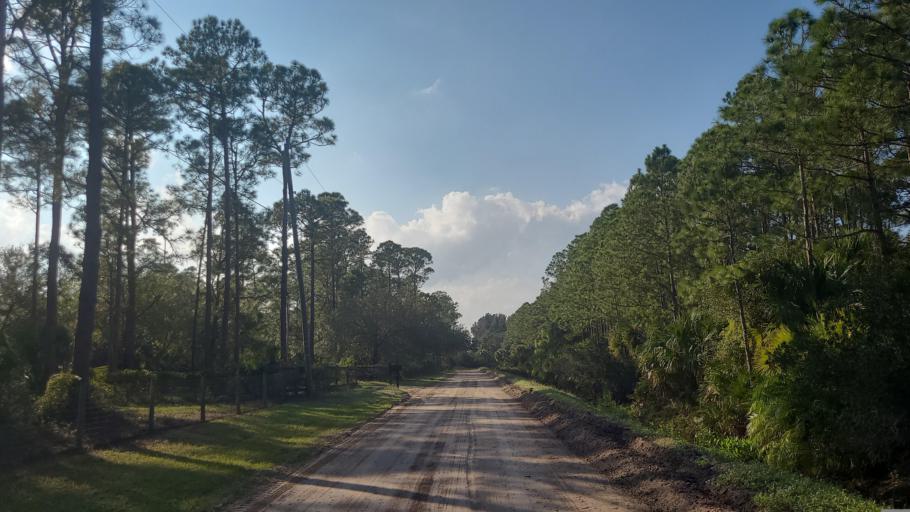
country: US
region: Florida
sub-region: Indian River County
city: Fellsmere
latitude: 27.7539
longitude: -80.6120
